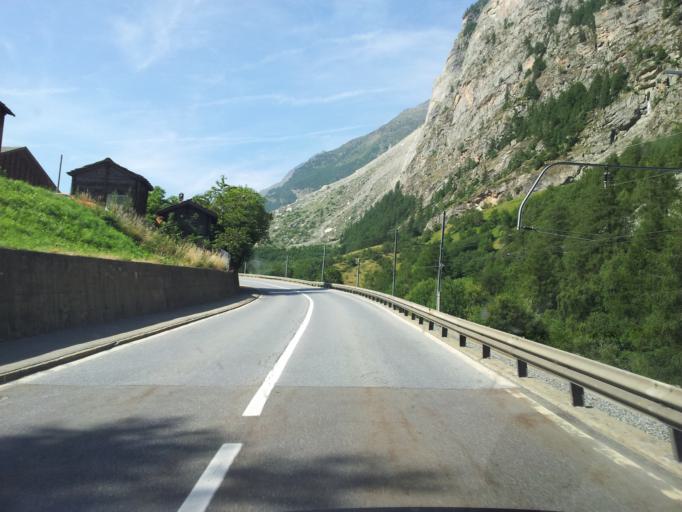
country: CH
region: Valais
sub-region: Visp District
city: Sankt Niklaus
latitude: 46.1244
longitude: 7.7888
